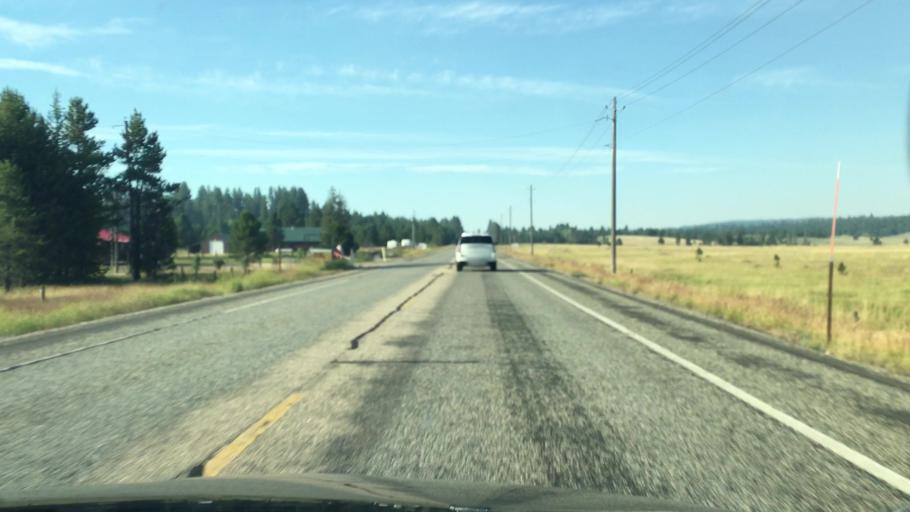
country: US
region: Idaho
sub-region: Valley County
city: Cascade
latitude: 44.3549
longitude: -116.0229
